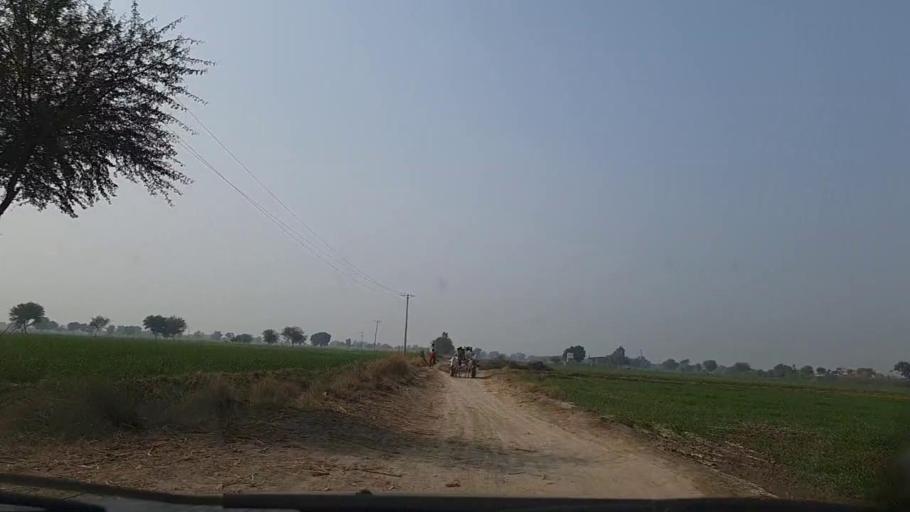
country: PK
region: Sindh
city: Sanghar
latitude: 26.0345
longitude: 68.9875
